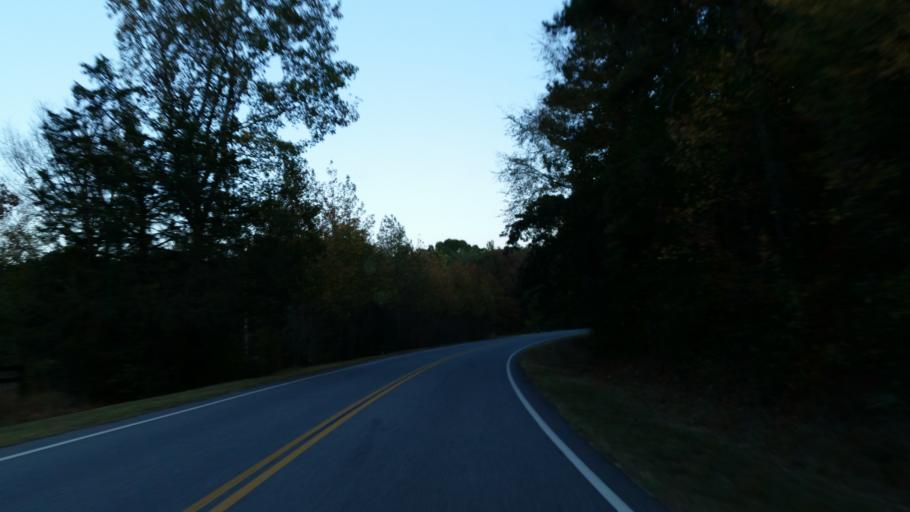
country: US
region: Georgia
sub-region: Gordon County
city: Calhoun
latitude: 34.6077
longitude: -85.0404
